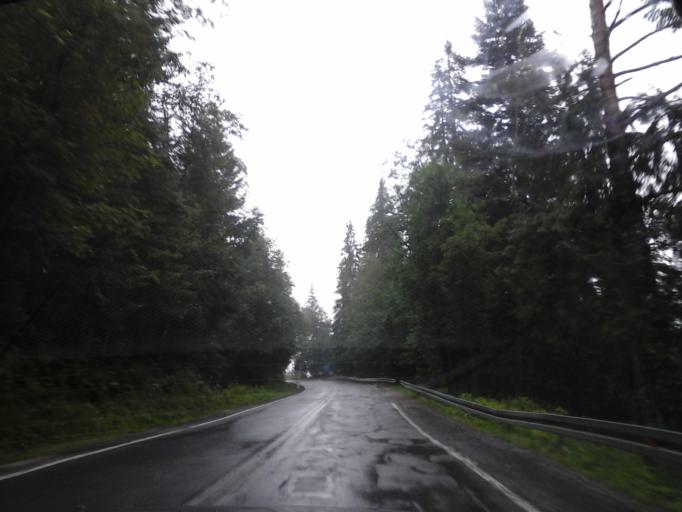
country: PL
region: Lesser Poland Voivodeship
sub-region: Powiat tatrzanski
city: Bukowina Tatrzanska
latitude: 49.2665
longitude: 20.1177
